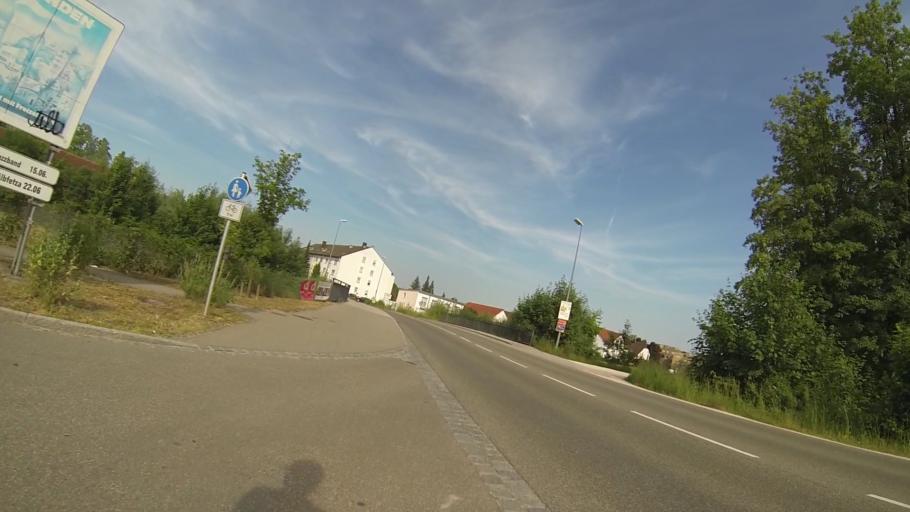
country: DE
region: Bavaria
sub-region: Swabia
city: Senden
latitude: 48.3240
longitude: 10.0264
